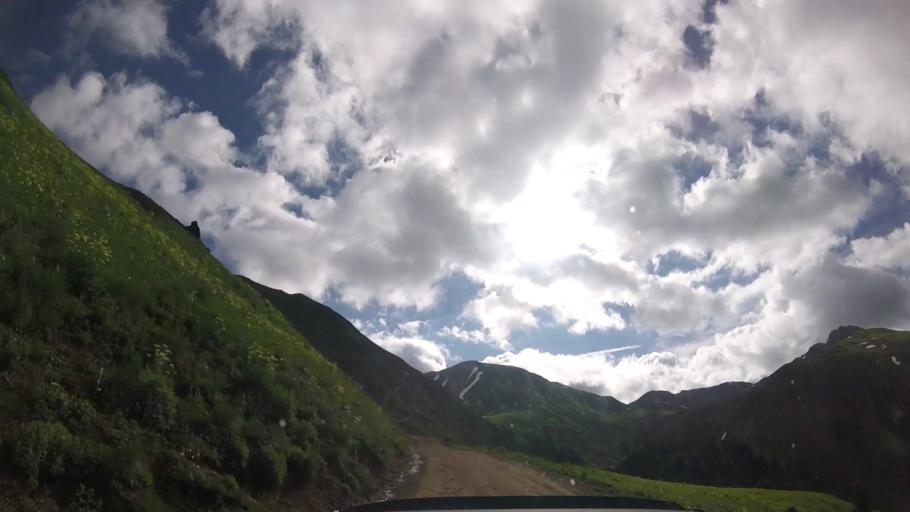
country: US
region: Colorado
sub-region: San Juan County
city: Silverton
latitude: 37.9121
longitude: -107.6440
